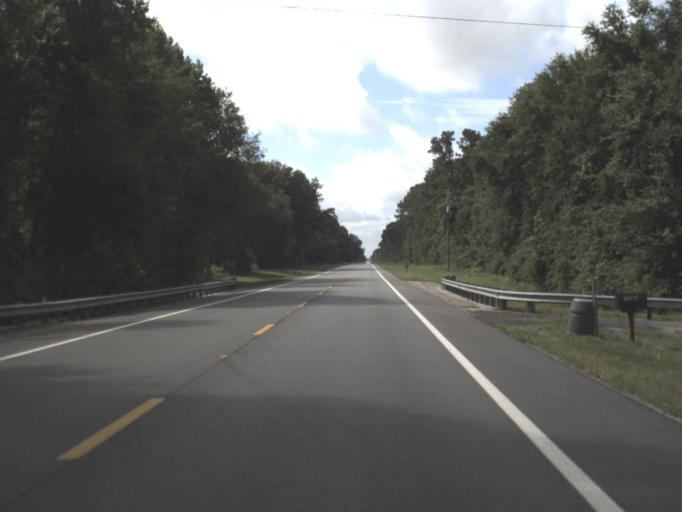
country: US
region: Florida
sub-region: Columbia County
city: Five Points
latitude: 30.4344
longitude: -82.6433
